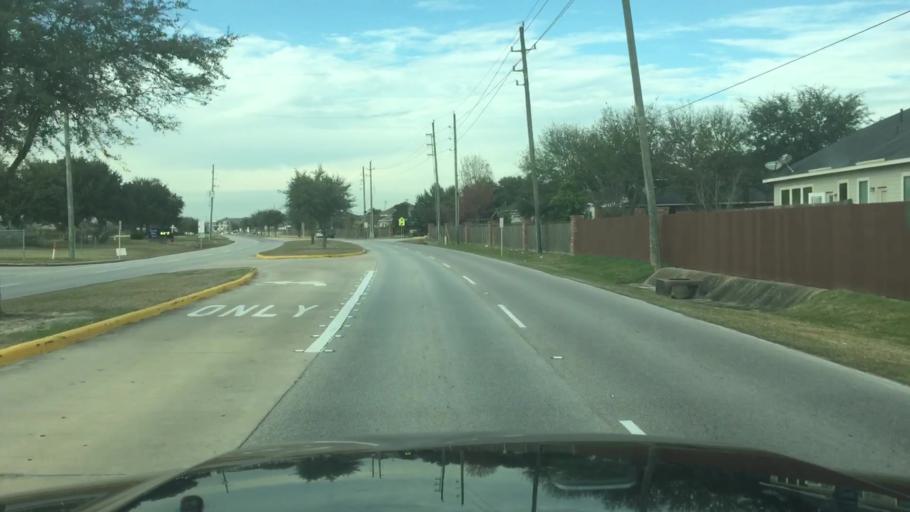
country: US
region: Texas
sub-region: Harris County
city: Oak Cliff Place
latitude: 29.8534
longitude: -95.6683
